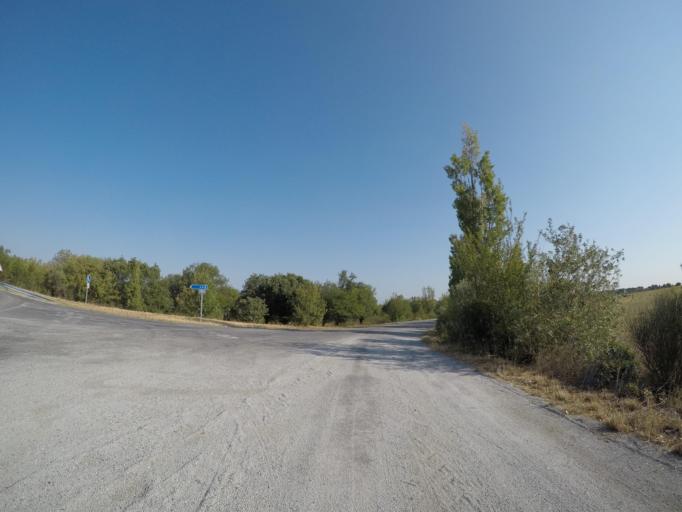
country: FR
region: Languedoc-Roussillon
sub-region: Departement des Pyrenees-Orientales
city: Pollestres
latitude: 42.6681
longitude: 2.8629
